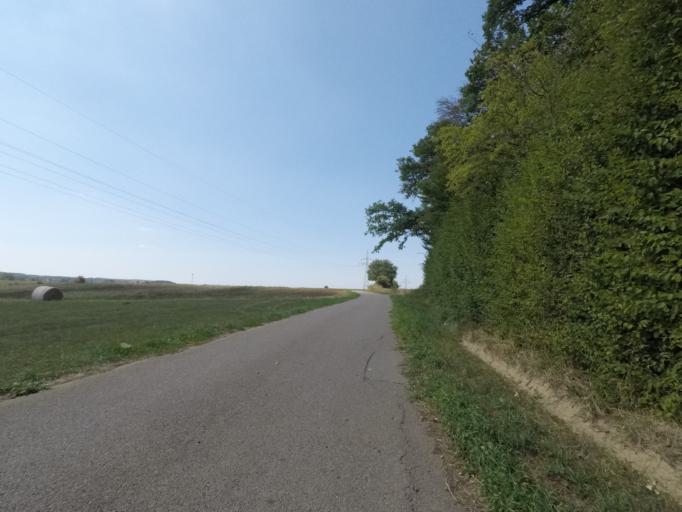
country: LU
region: Luxembourg
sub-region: Canton de Capellen
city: Mamer
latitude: 49.6233
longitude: 6.0007
